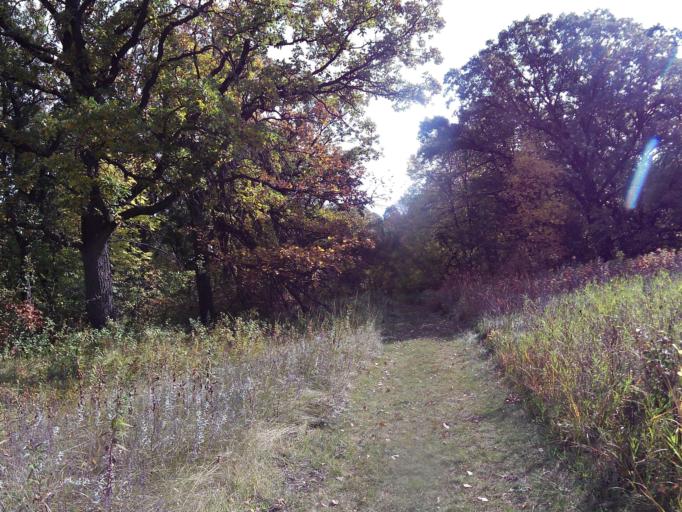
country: US
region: North Dakota
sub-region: Pembina County
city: Cavalier
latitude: 48.7797
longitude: -97.7338
